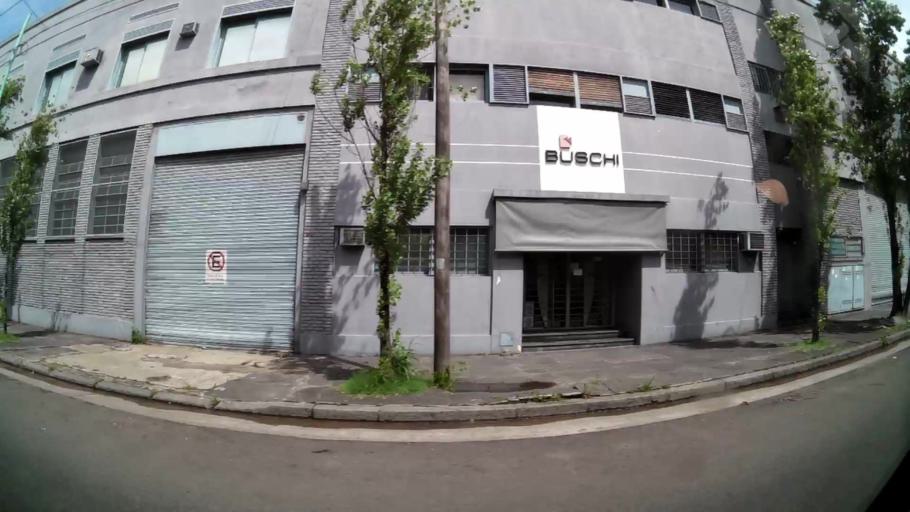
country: AR
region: Buenos Aires F.D.
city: Villa Lugano
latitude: -34.6618
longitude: -58.4266
